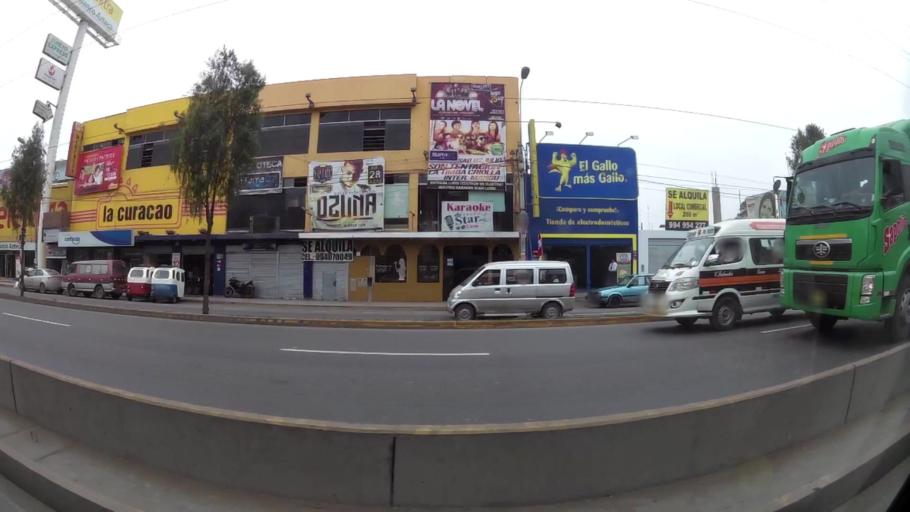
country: PE
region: Lima
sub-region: Lima
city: Punta Hermosa
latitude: -12.2751
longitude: -76.8716
